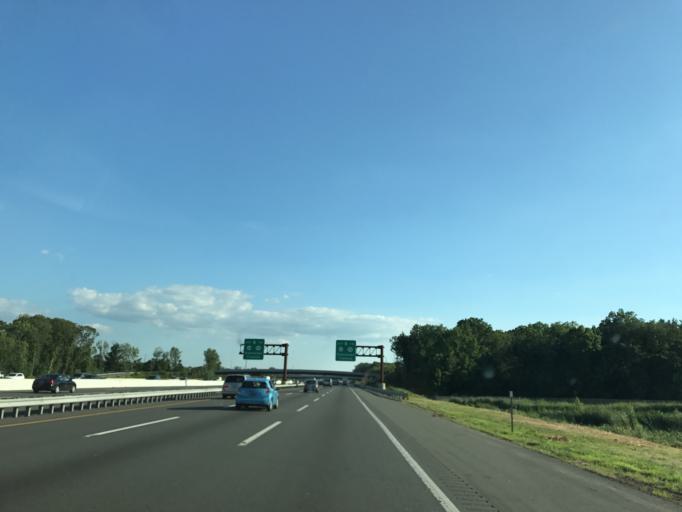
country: US
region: New Jersey
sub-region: Mercer County
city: Twin Rivers
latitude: 40.2828
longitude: -74.5041
